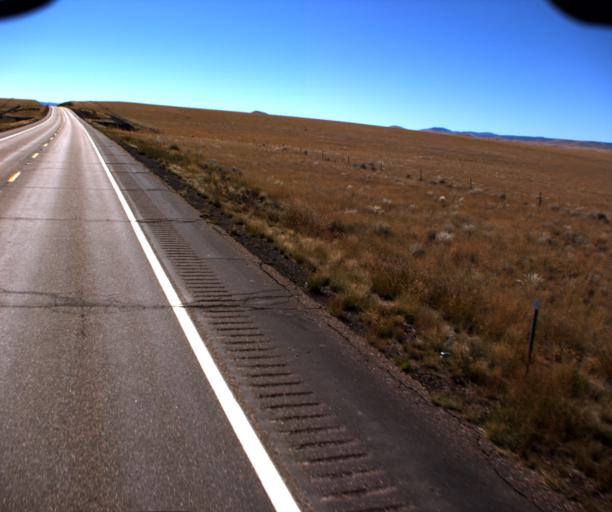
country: US
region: Arizona
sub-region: Apache County
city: Springerville
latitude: 34.3051
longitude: -109.3782
